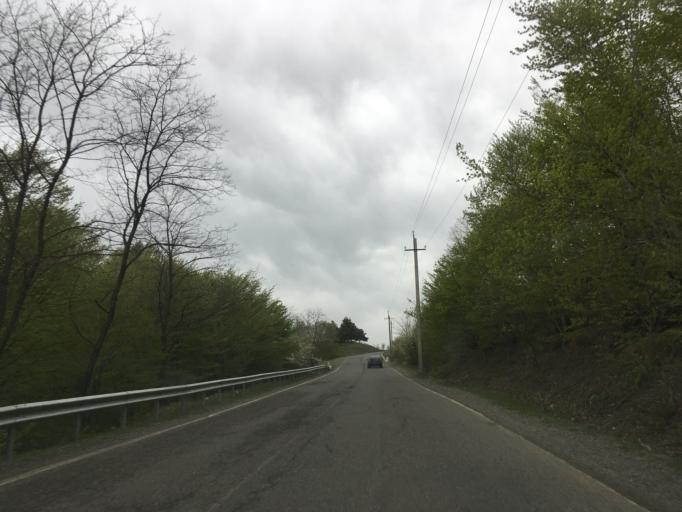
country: GE
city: Surami
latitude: 42.2122
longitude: 43.5214
